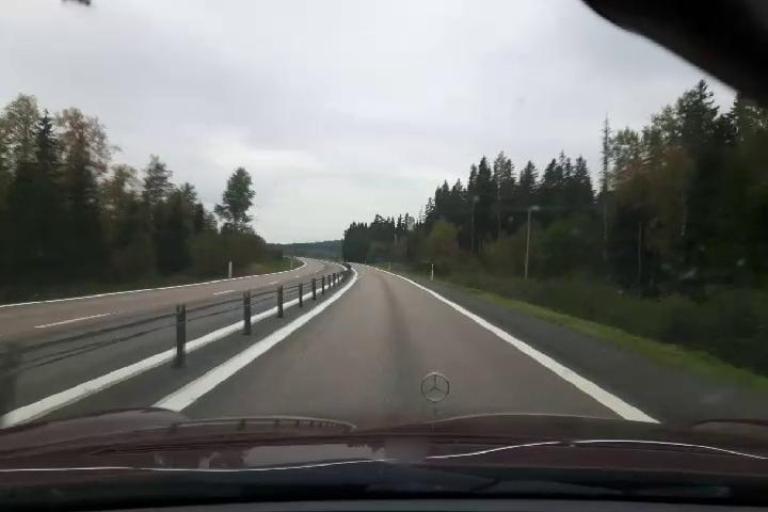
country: SE
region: Vaesternorrland
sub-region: Kramfors Kommun
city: Nordingra
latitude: 62.9085
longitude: 18.0927
